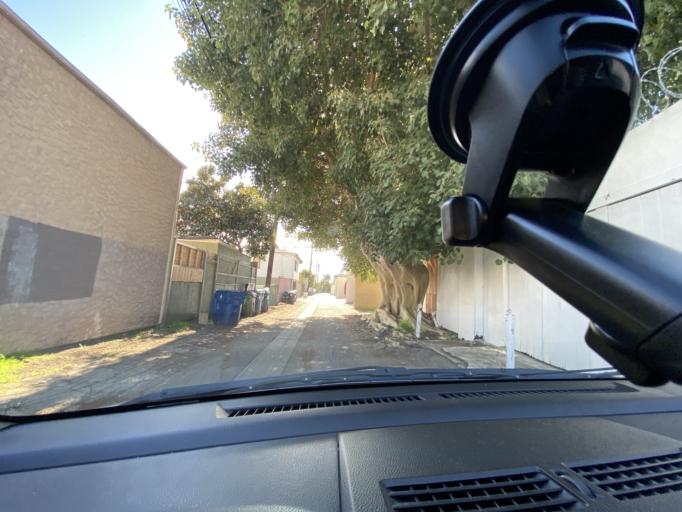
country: US
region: California
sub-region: Los Angeles County
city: Beverly Hills
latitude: 34.0499
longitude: -118.3839
